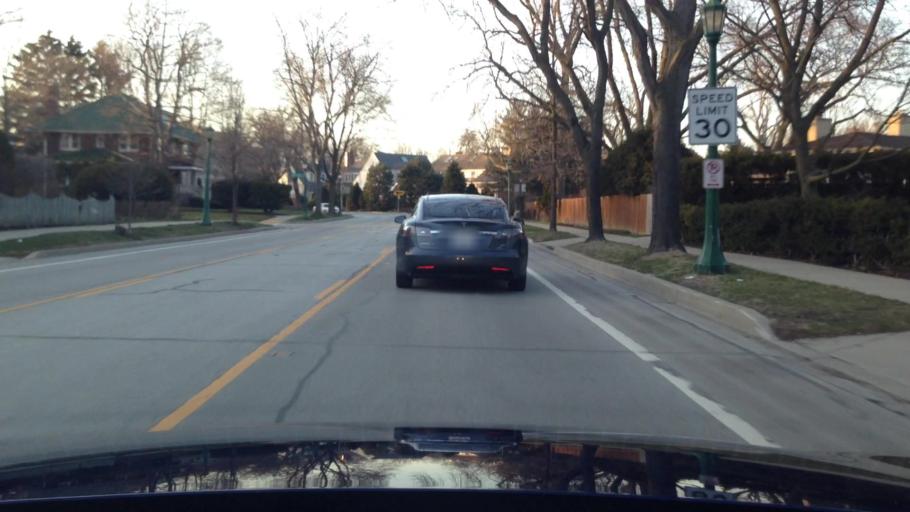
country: US
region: Illinois
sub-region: Cook County
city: Kenilworth
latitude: 42.0833
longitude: -87.6973
